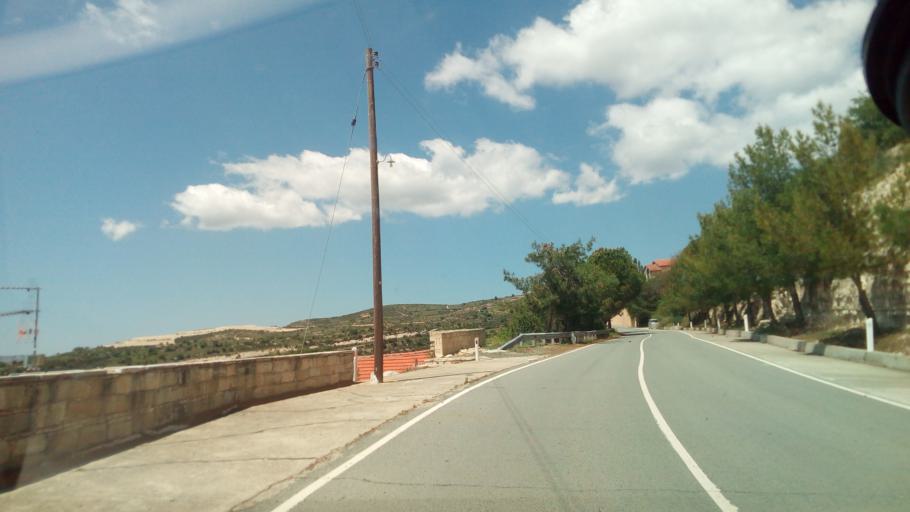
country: CY
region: Limassol
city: Pachna
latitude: 34.8402
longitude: 32.7711
